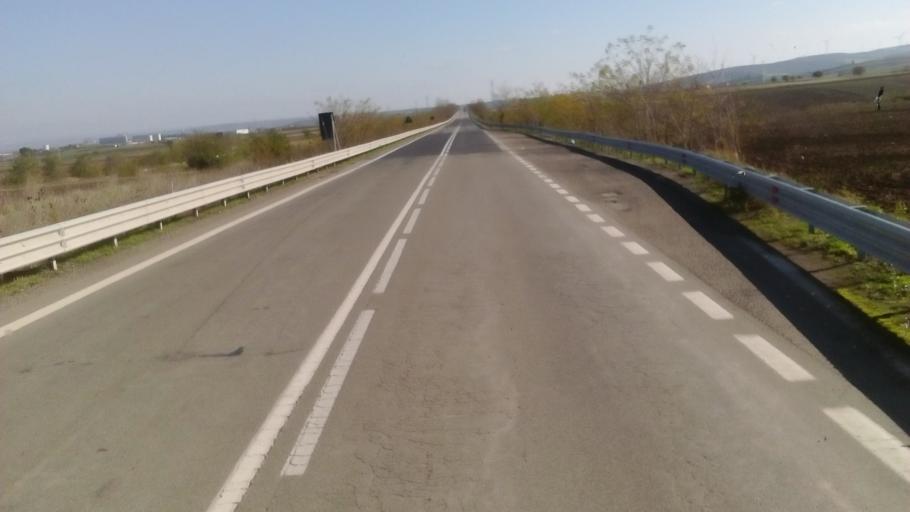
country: IT
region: Basilicate
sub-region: Provincia di Potenza
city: Zona 179
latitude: 41.0817
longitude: 15.6255
